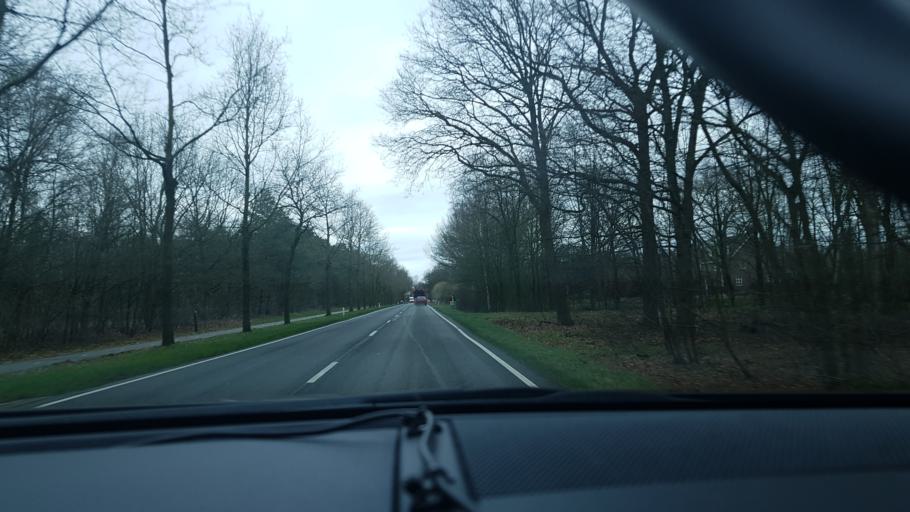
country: NL
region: Limburg
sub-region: Gemeente Leudal
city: Heythuysen
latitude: 51.3111
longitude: 5.8880
